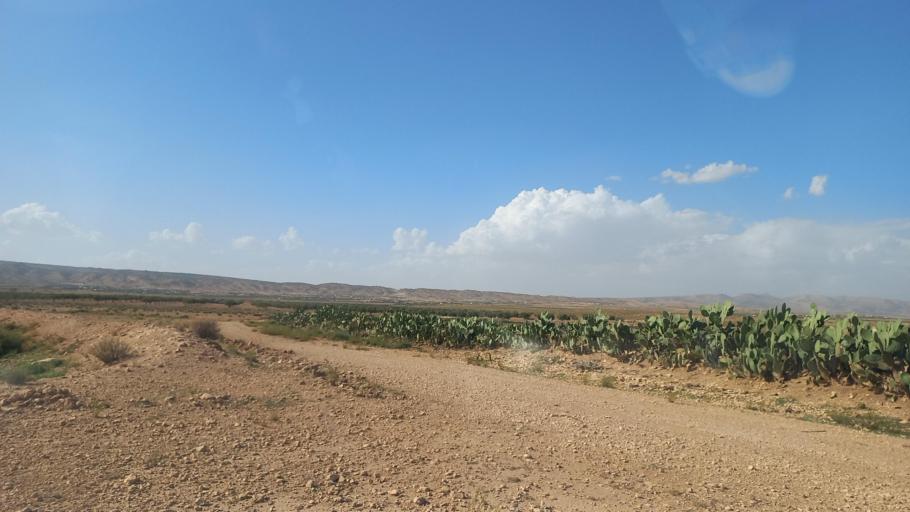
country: TN
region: Al Qasrayn
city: Kasserine
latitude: 35.3141
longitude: 9.0099
